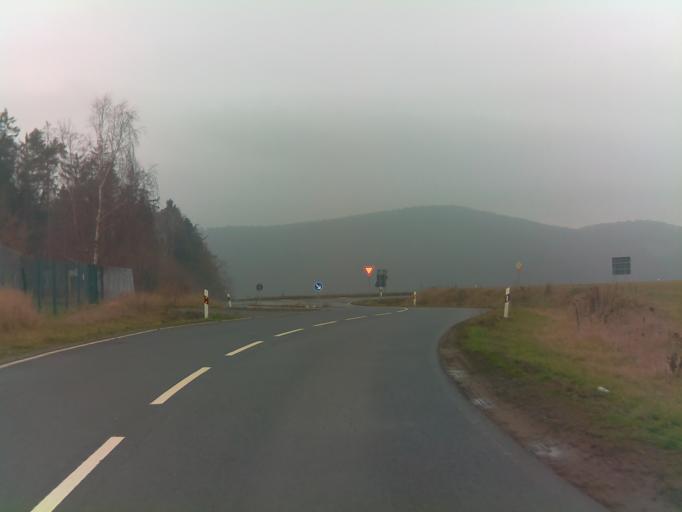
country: DE
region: Thuringia
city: Ehrenberg
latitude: 50.4796
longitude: 10.6519
